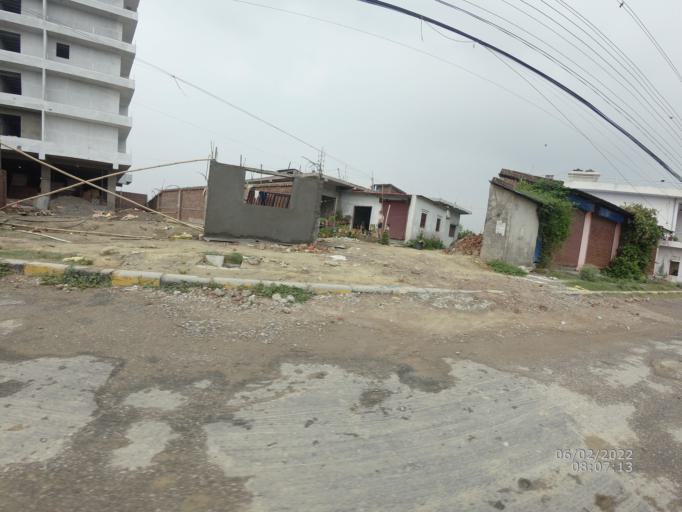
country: NP
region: Western Region
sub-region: Lumbini Zone
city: Bhairahawa
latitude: 27.4823
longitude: 83.4637
